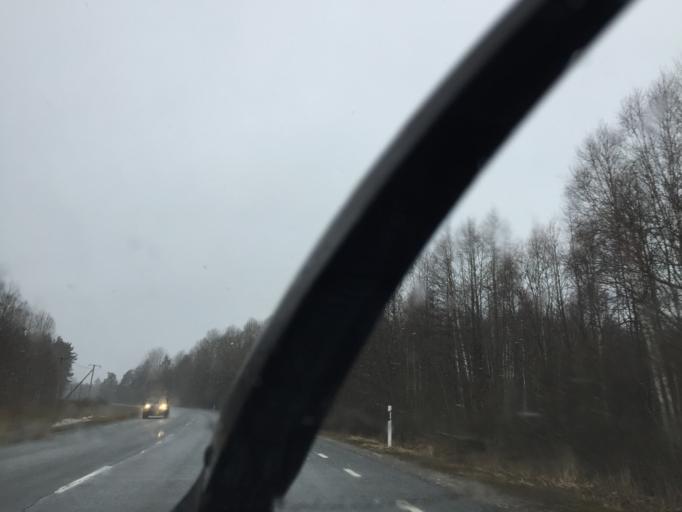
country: EE
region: Laeaene
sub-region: Ridala Parish
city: Uuemoisa
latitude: 58.8296
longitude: 23.7067
